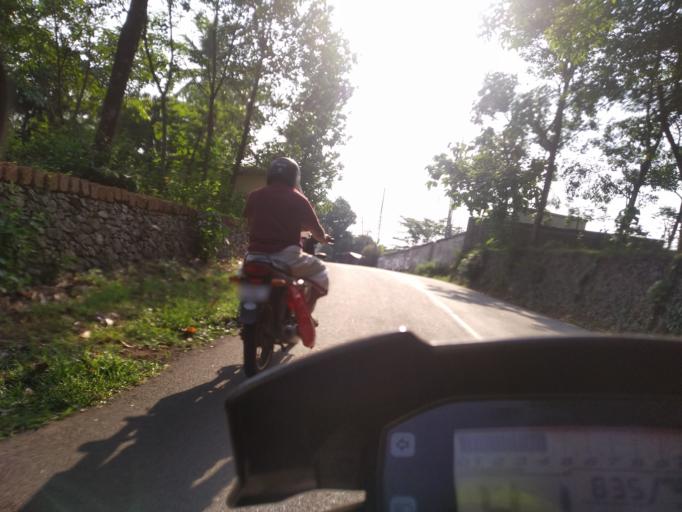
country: IN
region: Kerala
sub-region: Ernakulam
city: Ramamangalam
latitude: 9.9131
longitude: 76.4261
